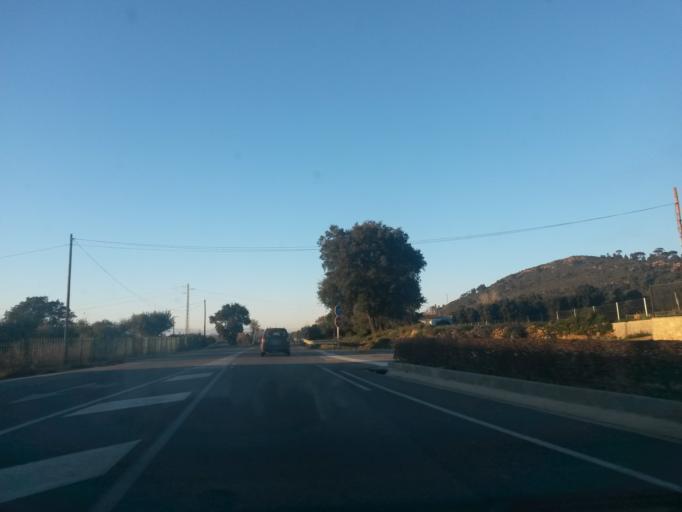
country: ES
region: Catalonia
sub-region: Provincia de Girona
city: Regencos
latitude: 41.9562
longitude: 3.1569
